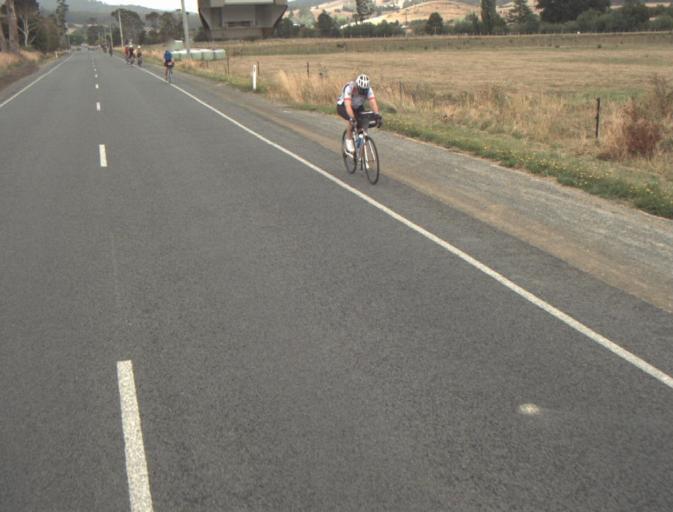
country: AU
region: Tasmania
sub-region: Launceston
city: Mayfield
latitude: -41.2389
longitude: 147.2157
